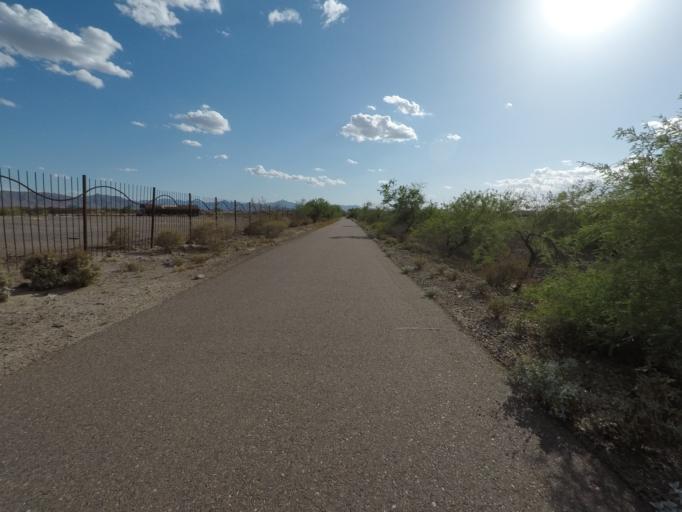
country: US
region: Arizona
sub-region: Maricopa County
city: Phoenix
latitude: 33.4192
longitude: -112.0790
